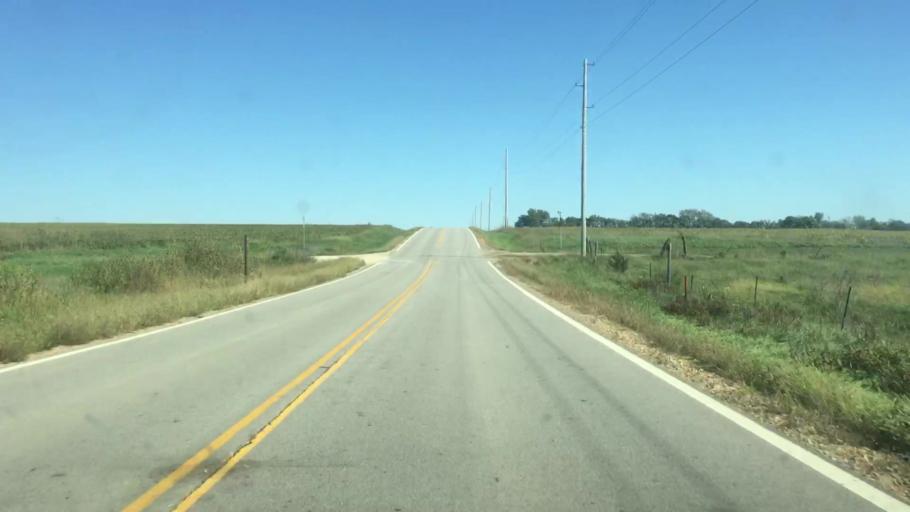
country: US
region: Kansas
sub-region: Jackson County
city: Holton
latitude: 39.5949
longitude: -95.6960
